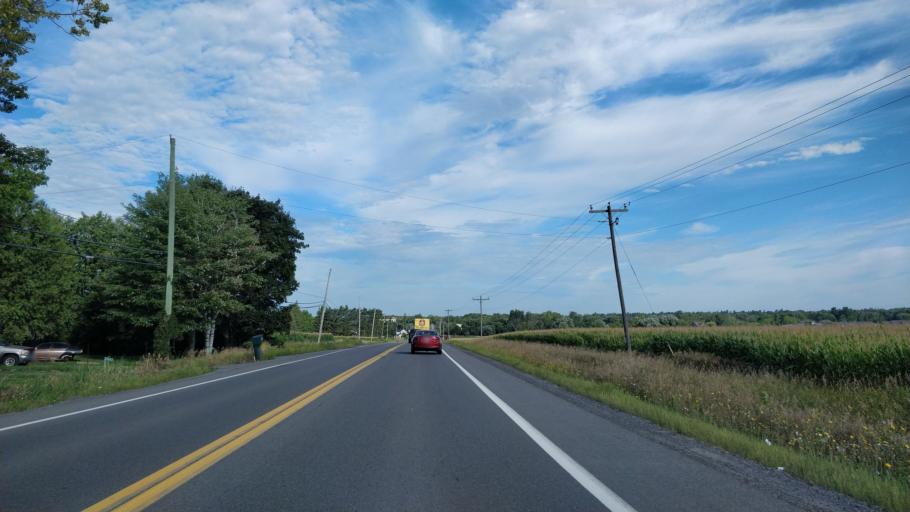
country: CA
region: Ontario
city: Bells Corners
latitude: 45.3363
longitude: -76.0256
